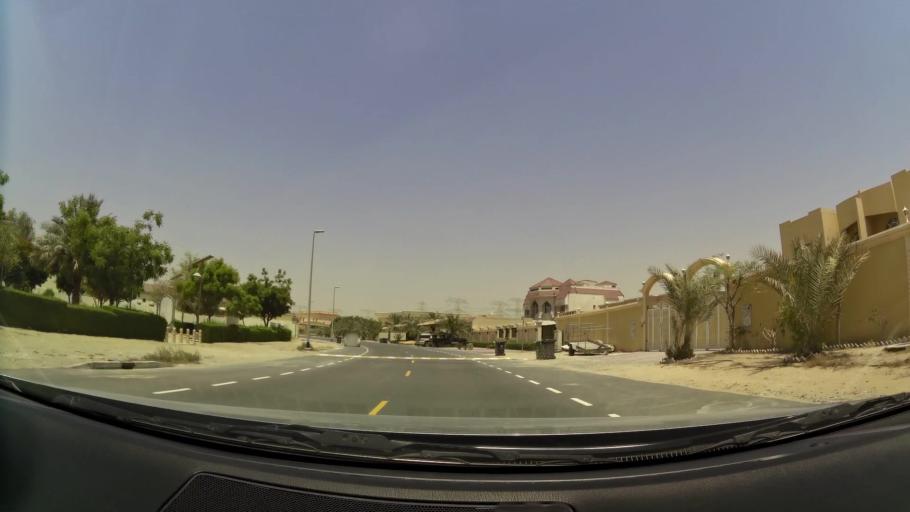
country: AE
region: Dubai
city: Dubai
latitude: 25.0821
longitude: 55.2074
